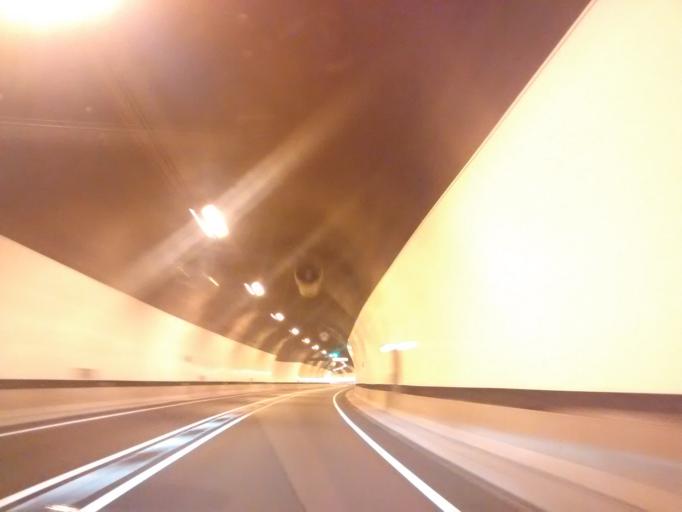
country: ES
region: Catalonia
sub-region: Provincia de Lleida
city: Coll de Nargo
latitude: 42.1320
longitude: 1.3094
